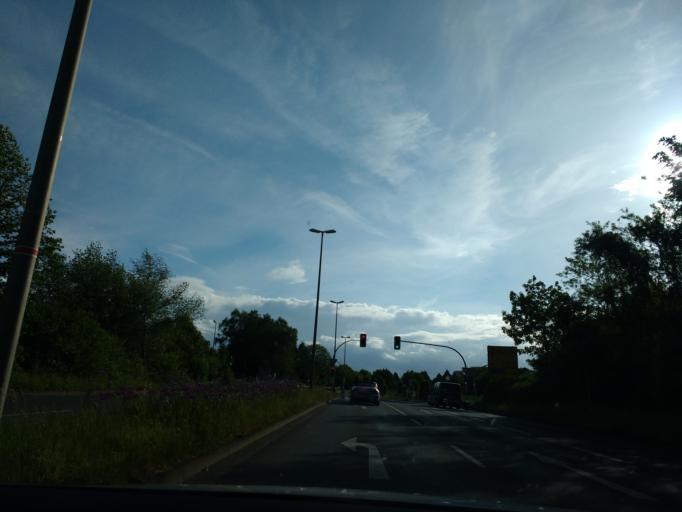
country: DE
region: North Rhine-Westphalia
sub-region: Regierungsbezirk Detmold
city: Bad Salzuflen
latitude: 52.0683
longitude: 8.7400
